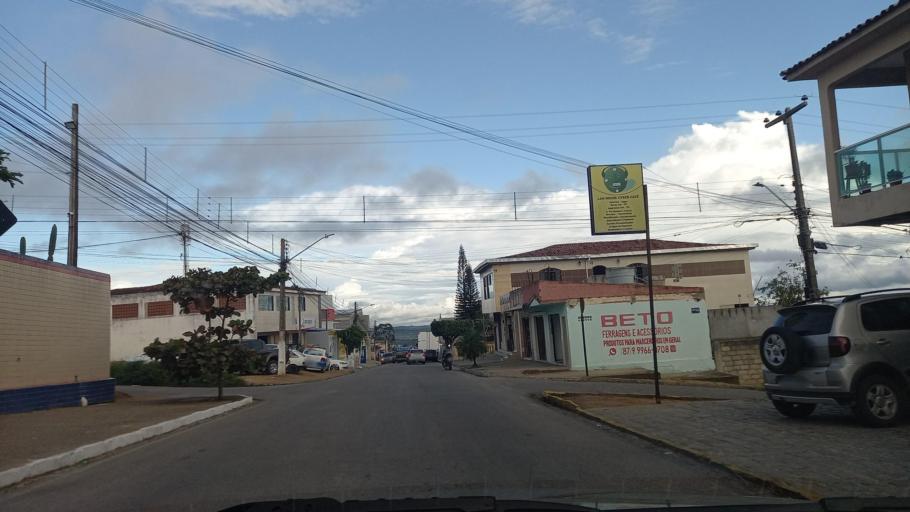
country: BR
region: Pernambuco
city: Garanhuns
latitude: -8.9025
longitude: -36.4923
